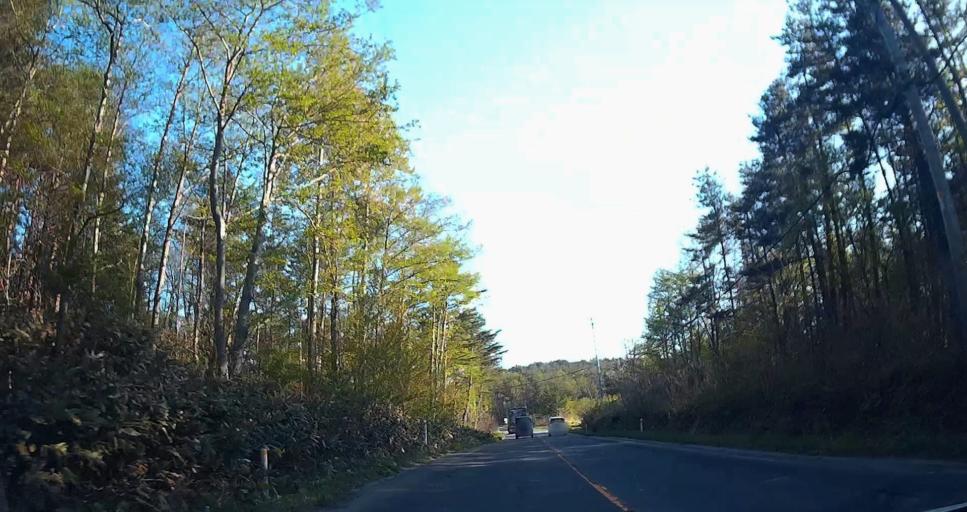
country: JP
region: Aomori
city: Mutsu
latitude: 41.3402
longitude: 141.2146
